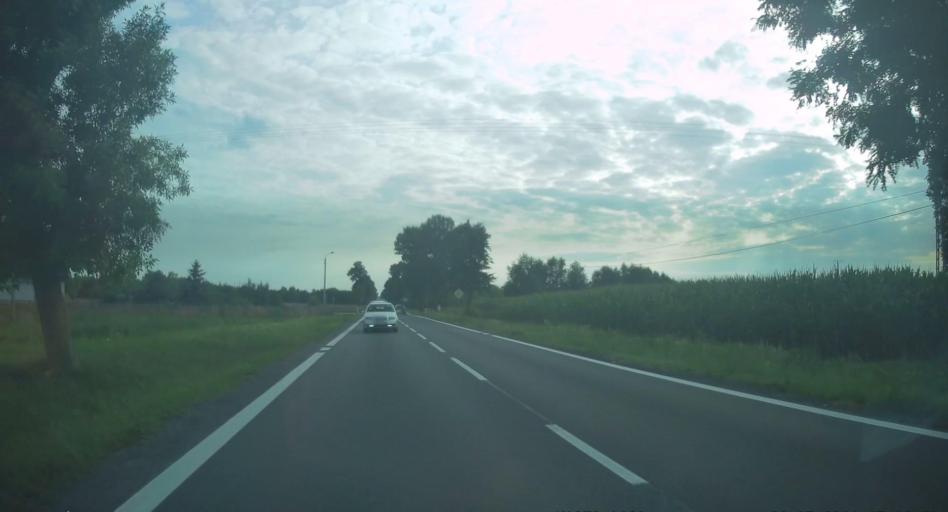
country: PL
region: Silesian Voivodeship
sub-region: Powiat czestochowski
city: Borowno
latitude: 50.8992
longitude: 19.2839
